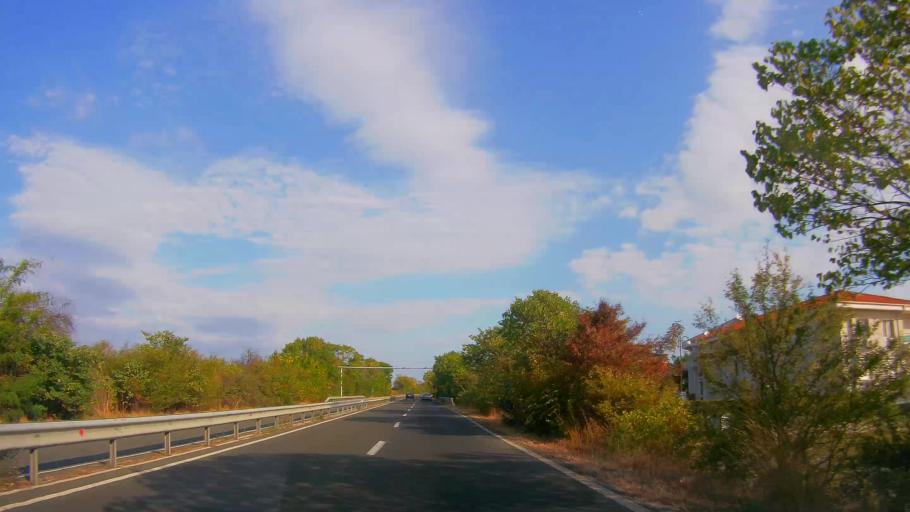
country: BG
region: Burgas
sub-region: Obshtina Sozopol
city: Chernomorets
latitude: 42.4312
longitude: 27.6390
